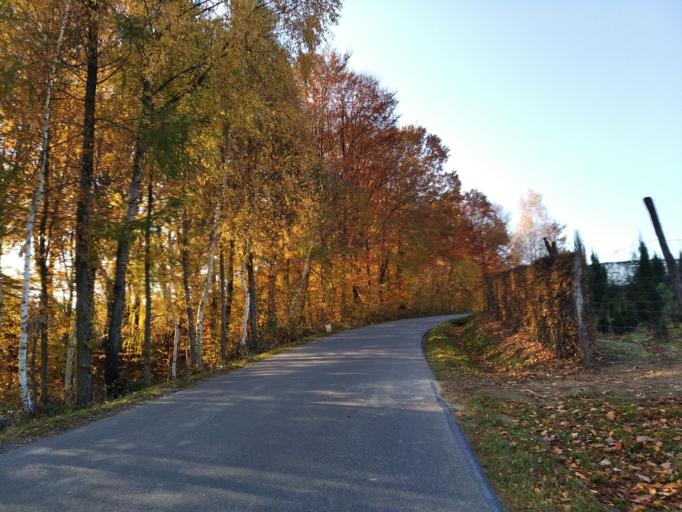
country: PL
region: Subcarpathian Voivodeship
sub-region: Powiat strzyzowski
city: Polomia
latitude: 49.8952
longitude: 21.8781
